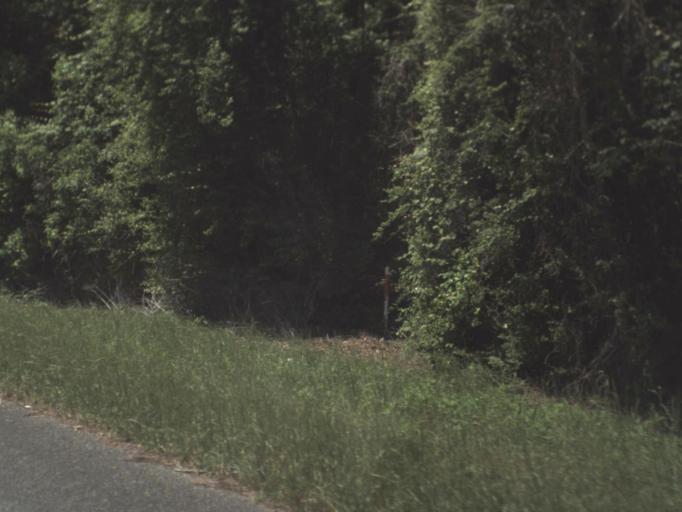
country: US
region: Florida
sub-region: Jefferson County
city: Monticello
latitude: 30.6562
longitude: -83.8773
